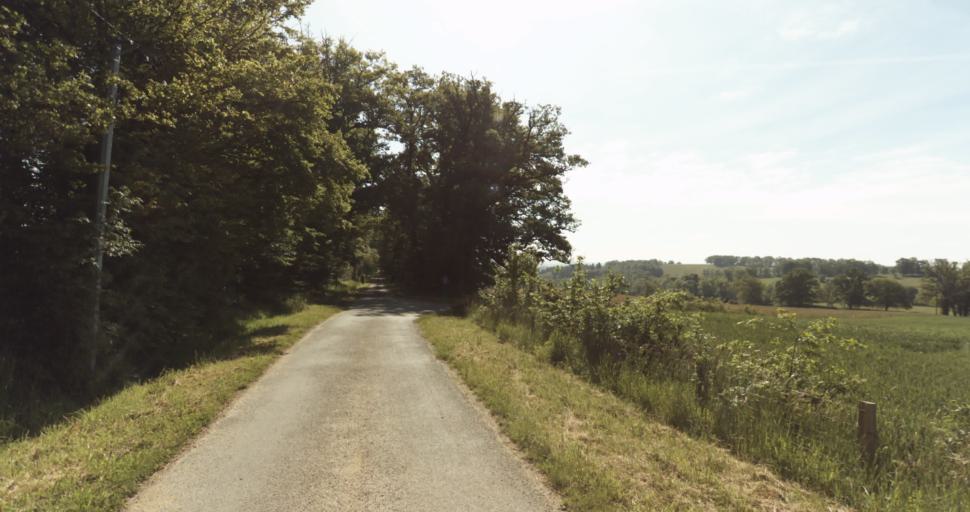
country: FR
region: Limousin
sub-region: Departement de la Haute-Vienne
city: Solignac
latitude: 45.7109
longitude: 1.2696
